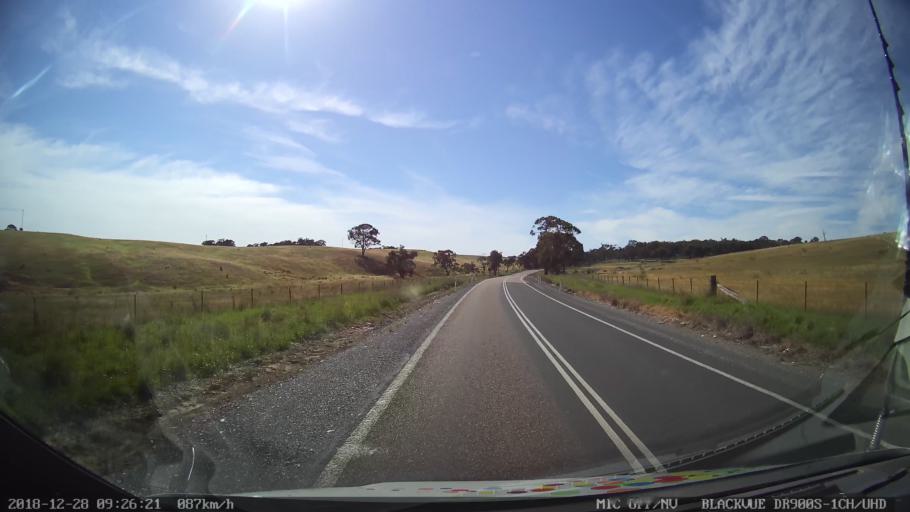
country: AU
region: New South Wales
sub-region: Upper Lachlan Shire
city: Crookwell
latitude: -34.4179
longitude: 149.3999
